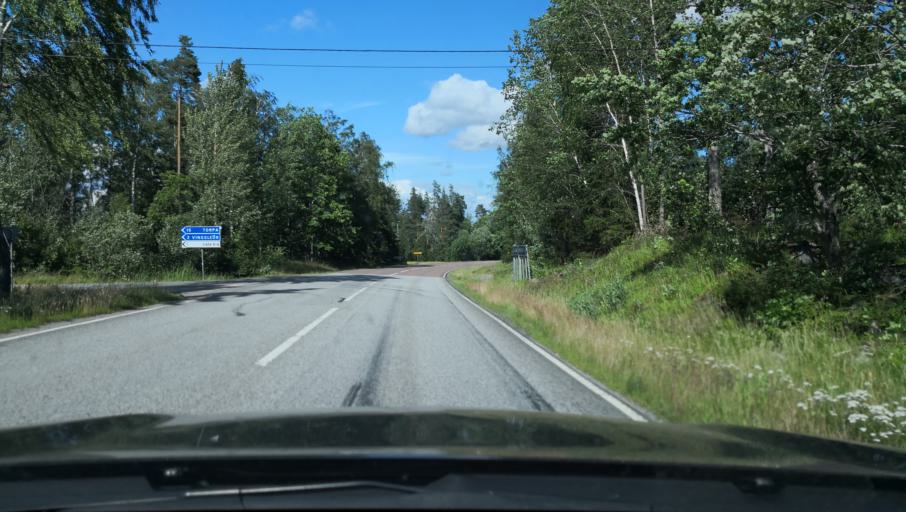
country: SE
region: Soedermanland
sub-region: Eskilstuna Kommun
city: Kvicksund
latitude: 59.3145
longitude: 16.2728
